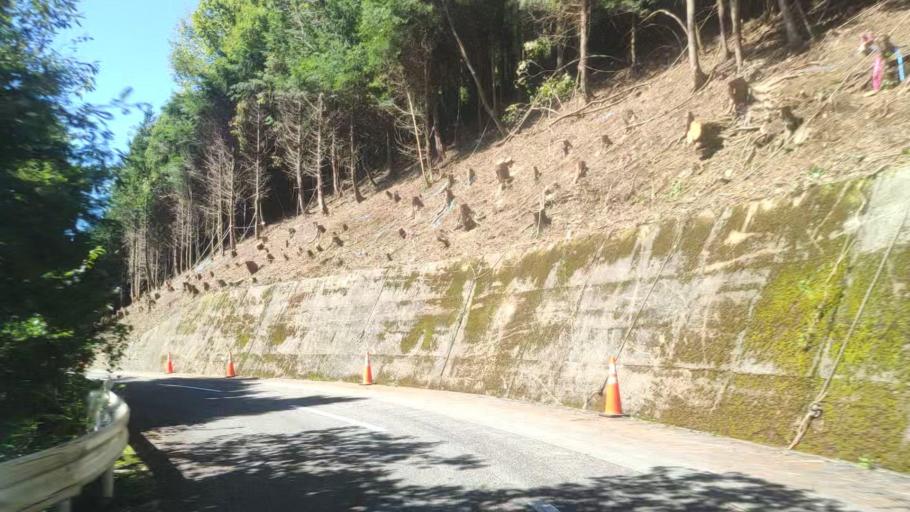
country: JP
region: Yamanashi
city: Fujikawaguchiko
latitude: 35.5685
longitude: 138.7844
